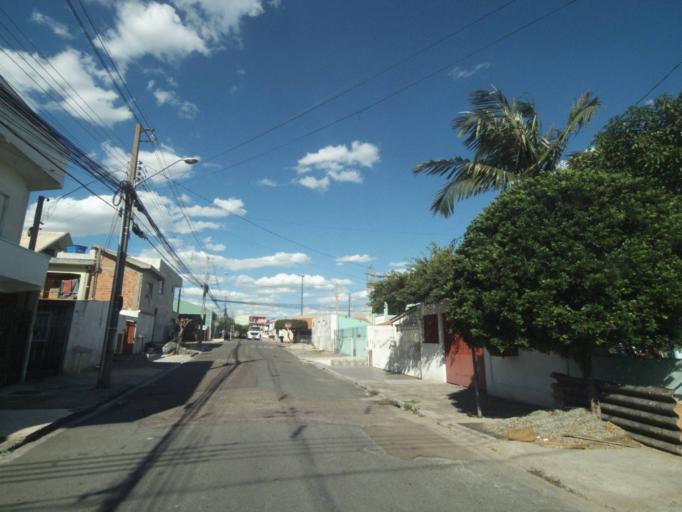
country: BR
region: Parana
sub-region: Curitiba
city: Curitiba
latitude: -25.5122
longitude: -49.3350
